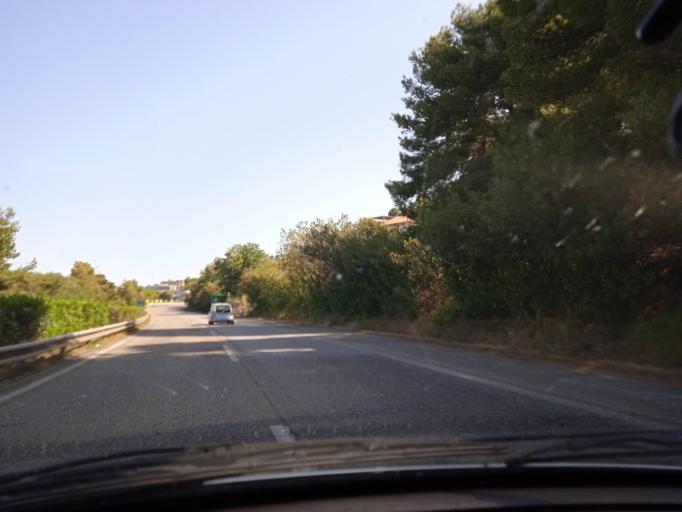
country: IT
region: Sicily
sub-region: Messina
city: Capo d'Orlando
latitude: 38.1332
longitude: 14.7367
